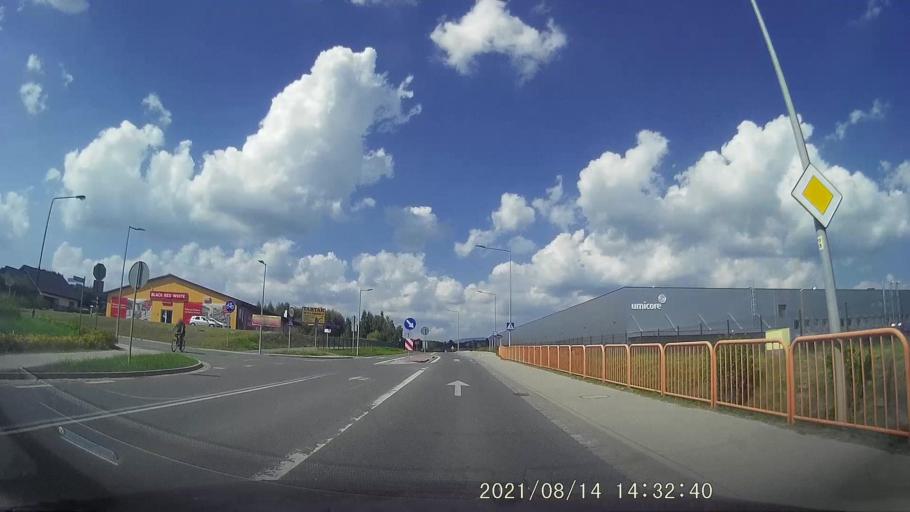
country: PL
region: Lower Silesian Voivodeship
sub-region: Powiat klodzki
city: Bozkow
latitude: 50.5517
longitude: 16.5486
